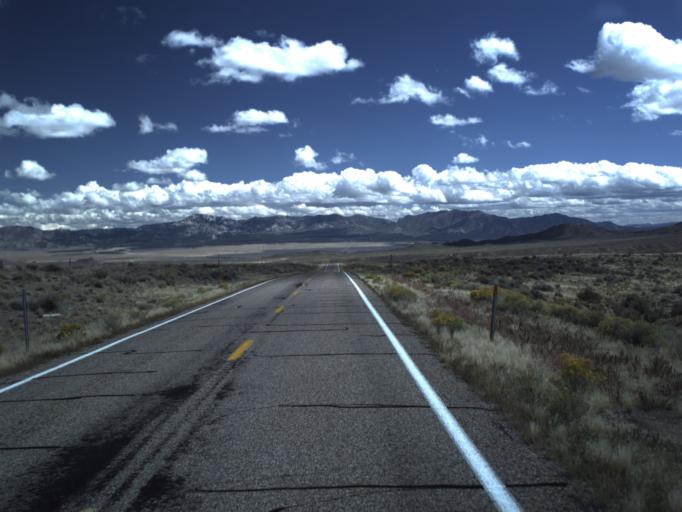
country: US
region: Utah
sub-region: Beaver County
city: Milford
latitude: 38.4459
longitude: -113.1829
